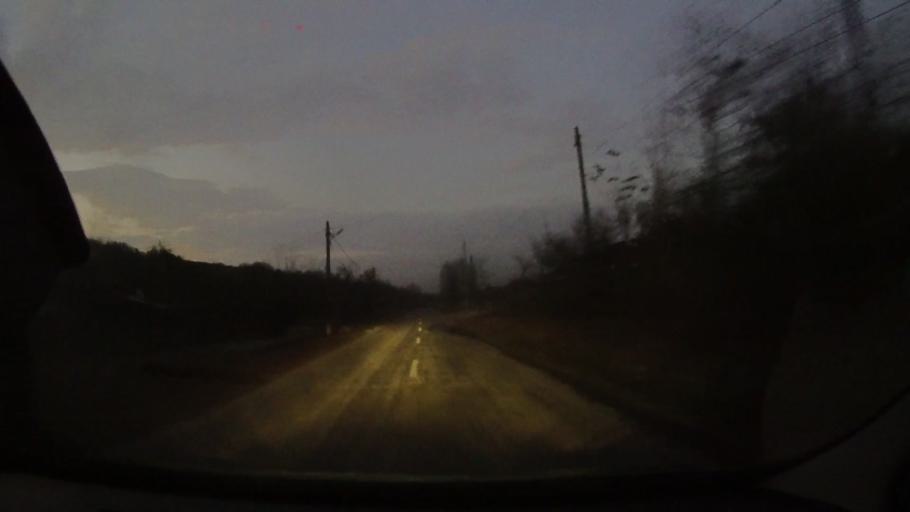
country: RO
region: Constanta
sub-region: Comuna Ion Corvin
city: Ion Corvin
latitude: 44.1406
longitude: 27.8341
